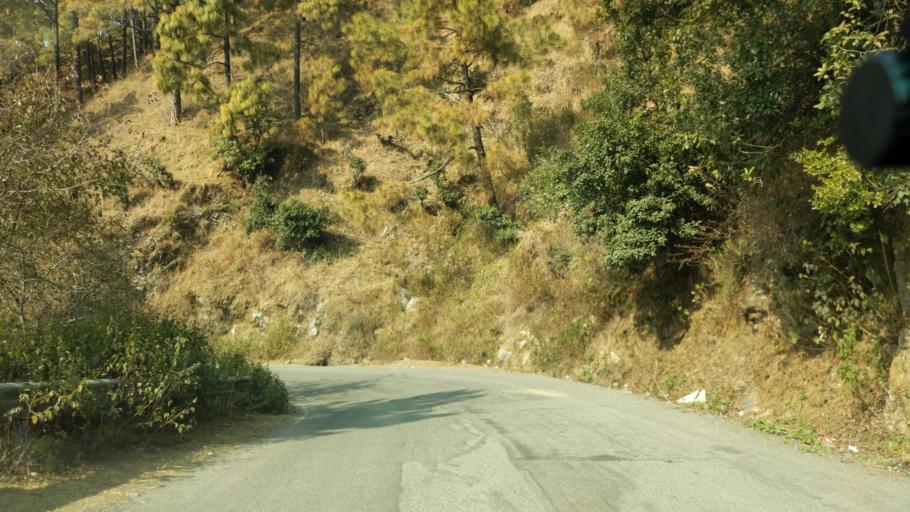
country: IN
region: Uttarakhand
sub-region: Naini Tal
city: Bhowali
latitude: 29.3906
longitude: 79.5360
